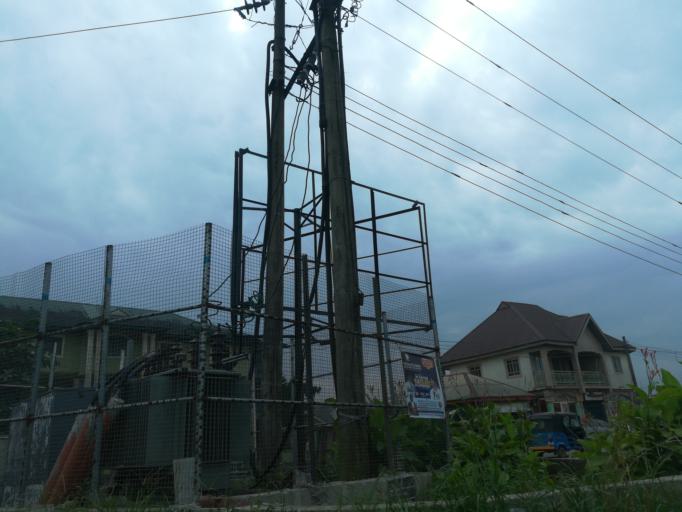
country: NG
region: Rivers
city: Port Harcourt
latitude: 4.8156
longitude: 6.9566
